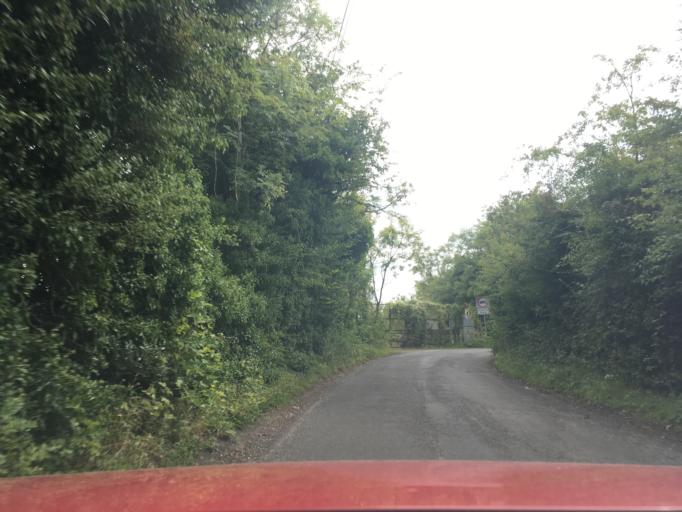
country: GB
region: England
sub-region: South Gloucestershire
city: Tytherington
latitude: 51.5966
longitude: -2.4984
